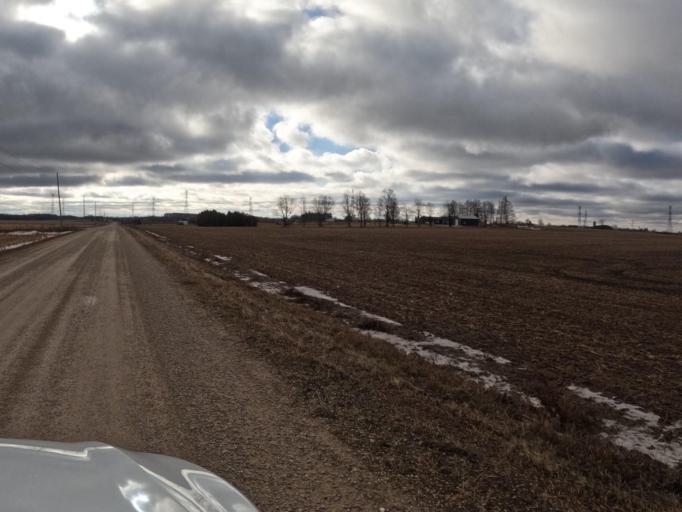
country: CA
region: Ontario
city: Shelburne
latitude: 43.9966
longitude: -80.3861
